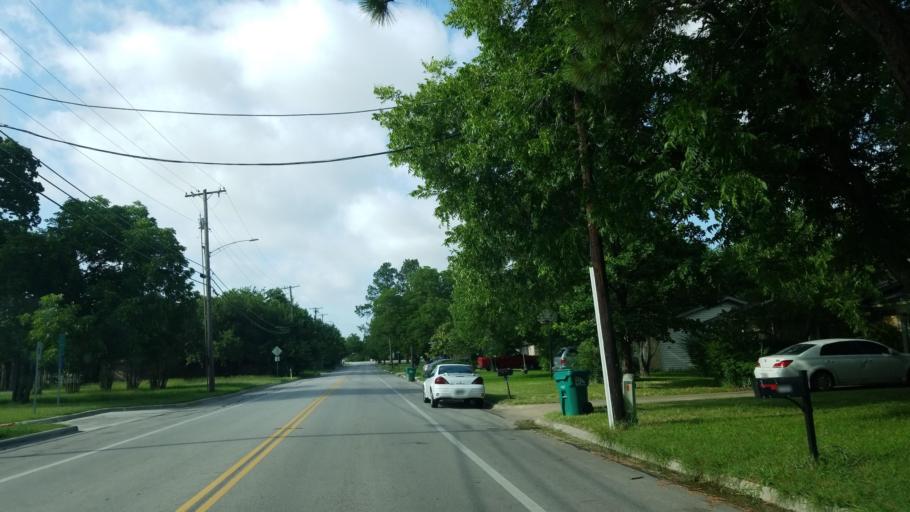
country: US
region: Texas
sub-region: Denton County
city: Denton
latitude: 33.2169
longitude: -97.0965
